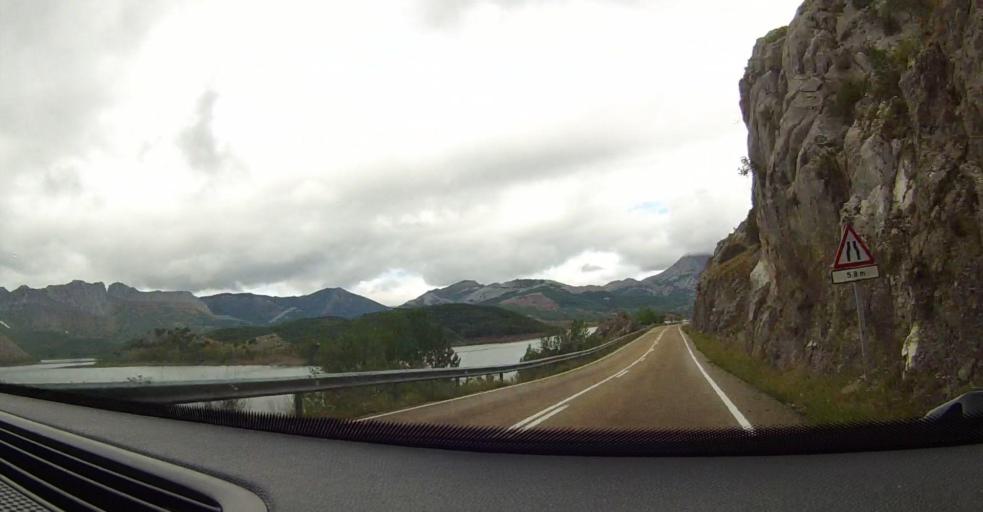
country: ES
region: Castille and Leon
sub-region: Provincia de Leon
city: Bonar
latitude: 42.9304
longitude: -5.2828
